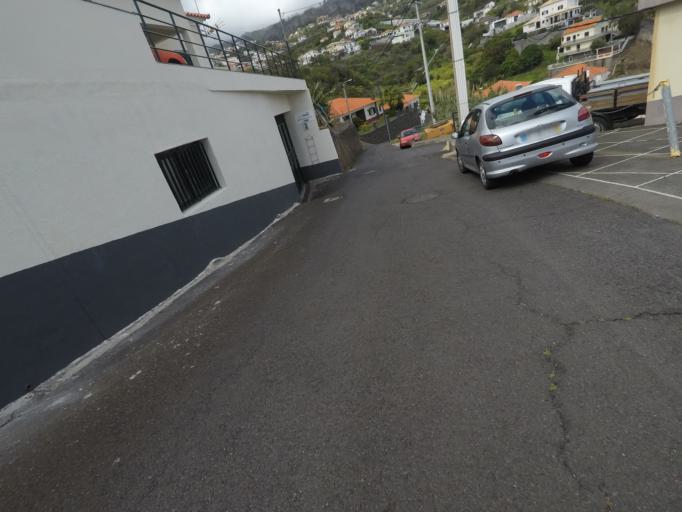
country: PT
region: Madeira
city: Calheta
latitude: 32.7266
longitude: -17.1783
